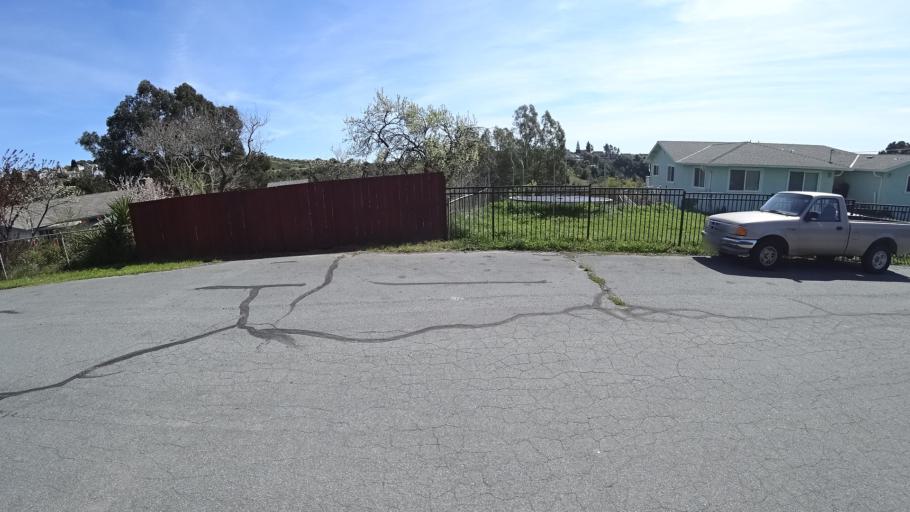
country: US
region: California
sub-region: Alameda County
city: Fairview
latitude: 37.6586
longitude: -122.0288
